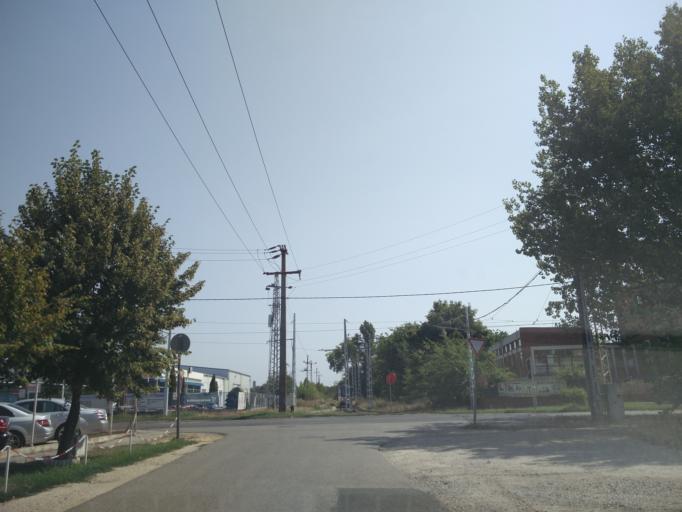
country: HU
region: Csongrad
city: Szeged
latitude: 46.2645
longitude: 20.1095
